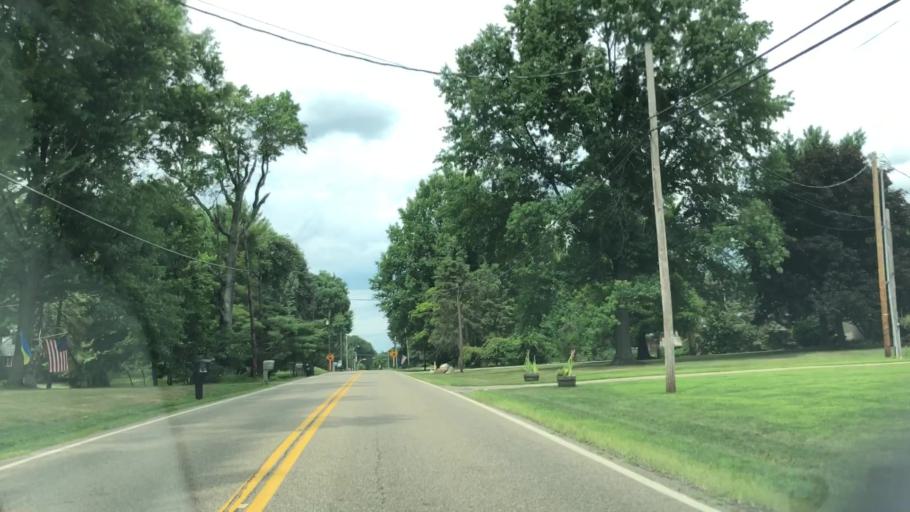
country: US
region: Ohio
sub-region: Summit County
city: Greensburg
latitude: 40.8906
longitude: -81.4595
